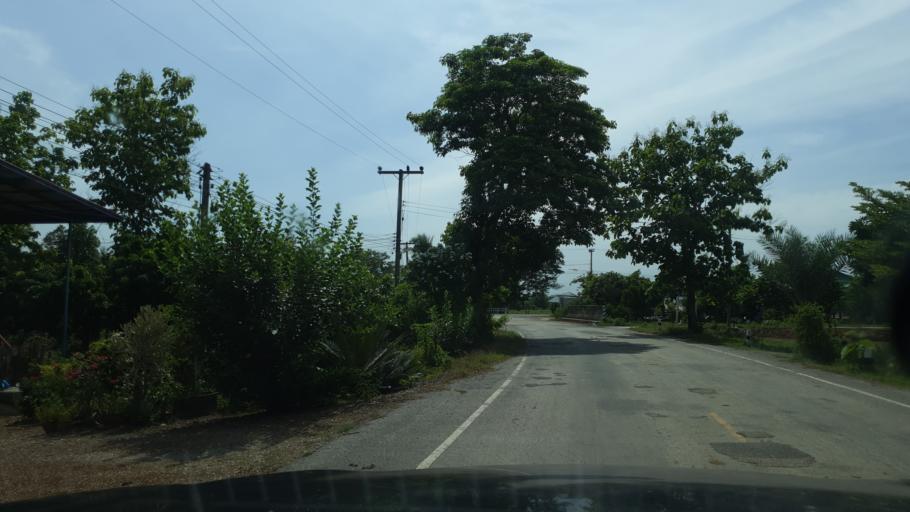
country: TH
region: Sukhothai
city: Si Samrong
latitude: 17.1945
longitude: 99.7368
